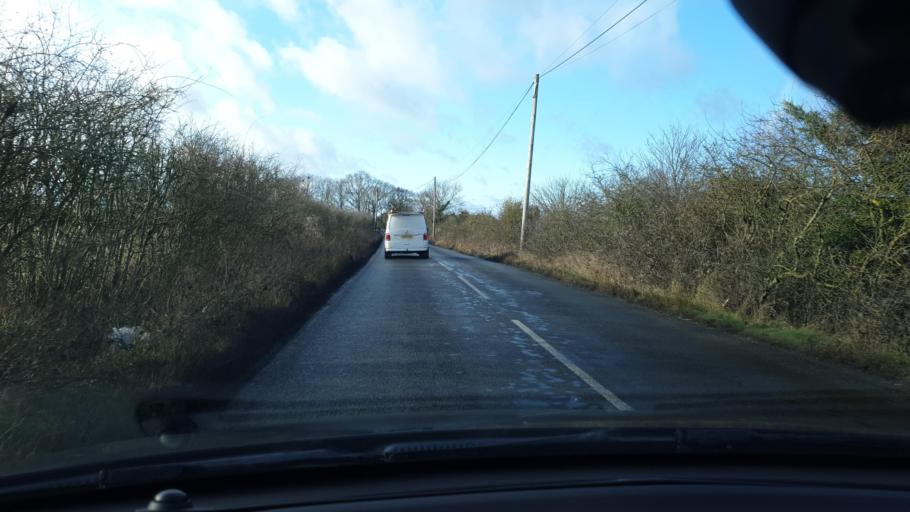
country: GB
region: England
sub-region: Essex
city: Little Clacton
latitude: 51.8256
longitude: 1.1692
